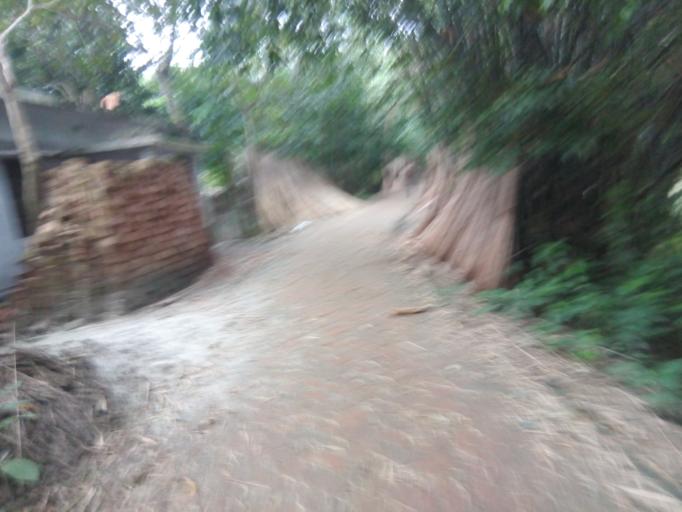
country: BD
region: Khulna
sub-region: Magura
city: Magura
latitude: 23.5050
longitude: 89.6096
